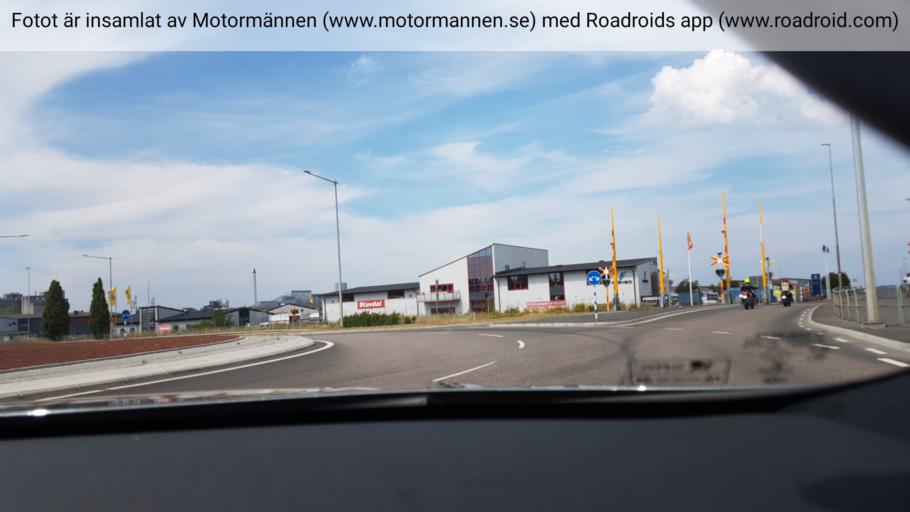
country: SE
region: Vaestra Goetaland
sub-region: Lidkopings Kommun
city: Lidkoping
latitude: 58.5000
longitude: 13.1803
